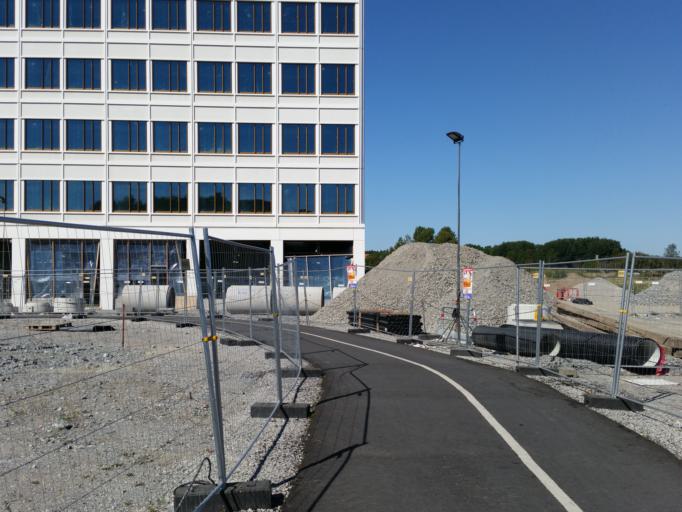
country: SE
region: Stockholm
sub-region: Solna Kommun
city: Solna
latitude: 59.3811
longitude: 18.0017
